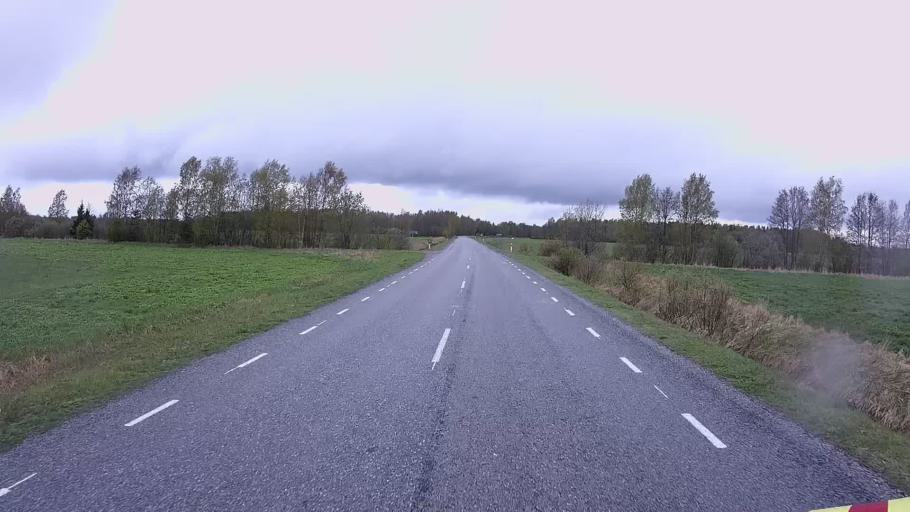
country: EE
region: Hiiumaa
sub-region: Kaerdla linn
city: Kardla
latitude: 58.7503
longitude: 22.5228
